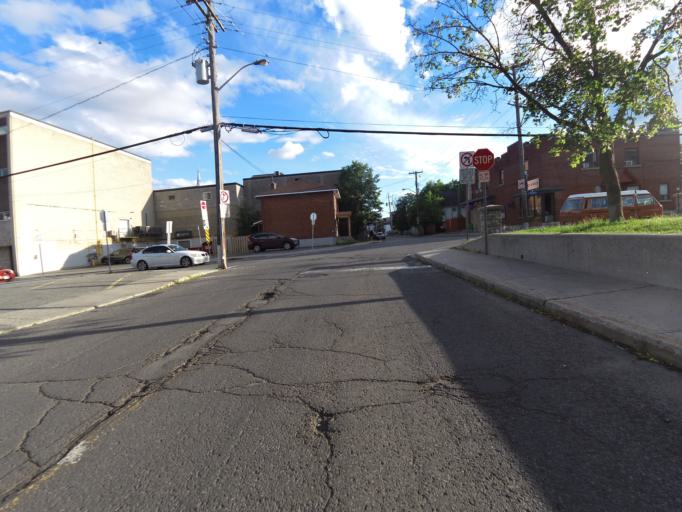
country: CA
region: Ontario
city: Ottawa
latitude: 45.4063
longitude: -75.7233
